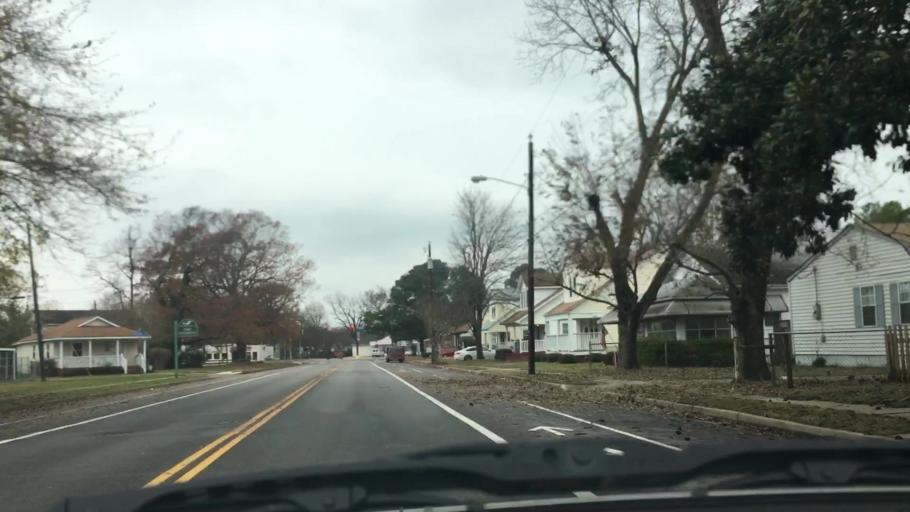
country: US
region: Virginia
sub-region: City of Norfolk
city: Norfolk
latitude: 36.8781
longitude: -76.2477
